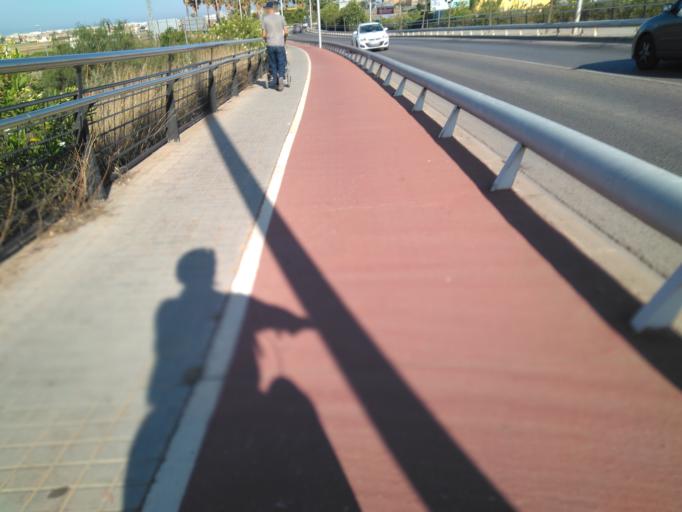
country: ES
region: Valencia
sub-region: Provincia de Valencia
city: Burjassot
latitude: 39.5035
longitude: -0.4011
